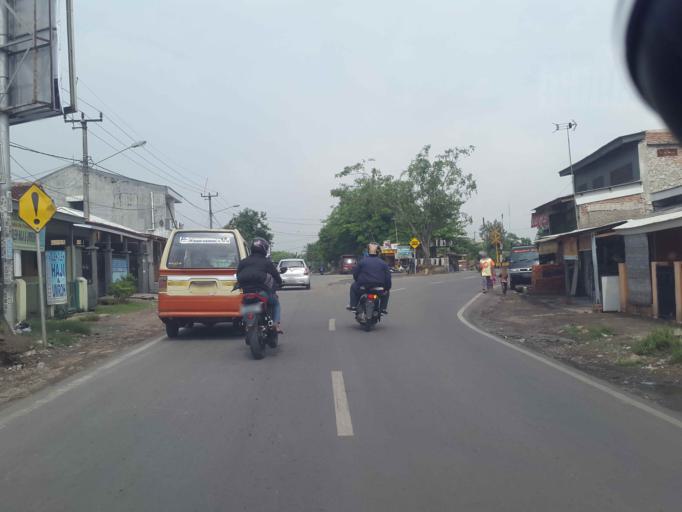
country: ID
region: West Java
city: Rengasdengklok
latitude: -6.2789
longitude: 107.2750
